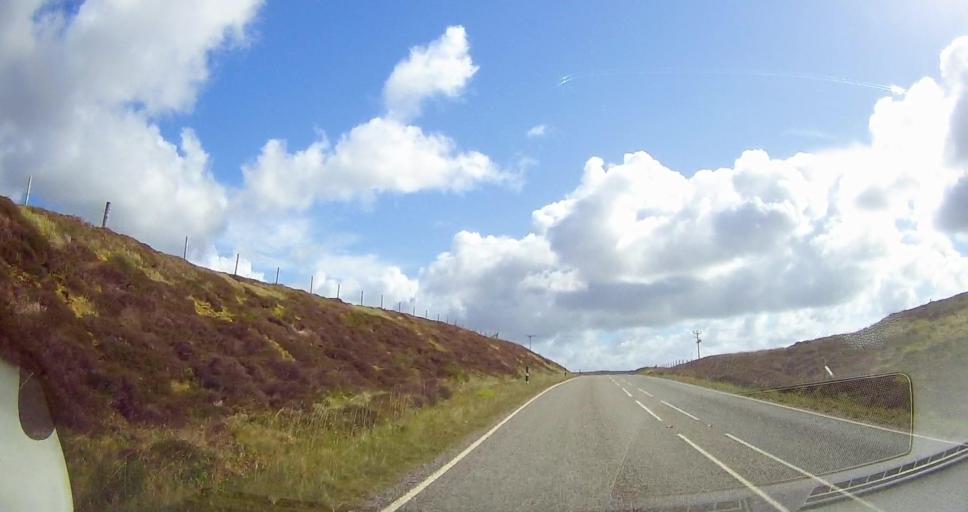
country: GB
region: Scotland
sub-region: Shetland Islands
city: Lerwick
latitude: 60.4711
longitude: -1.4069
